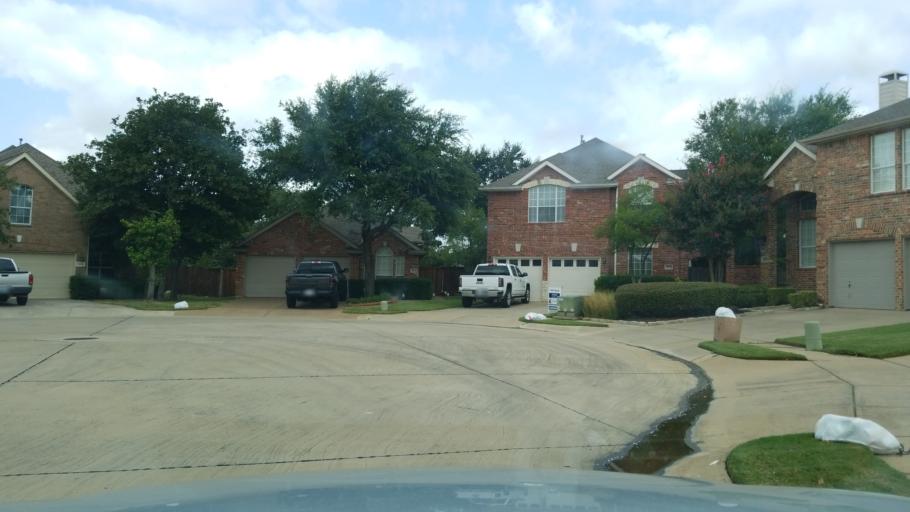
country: US
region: Texas
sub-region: Tarrant County
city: Euless
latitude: 32.8425
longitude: -97.1051
